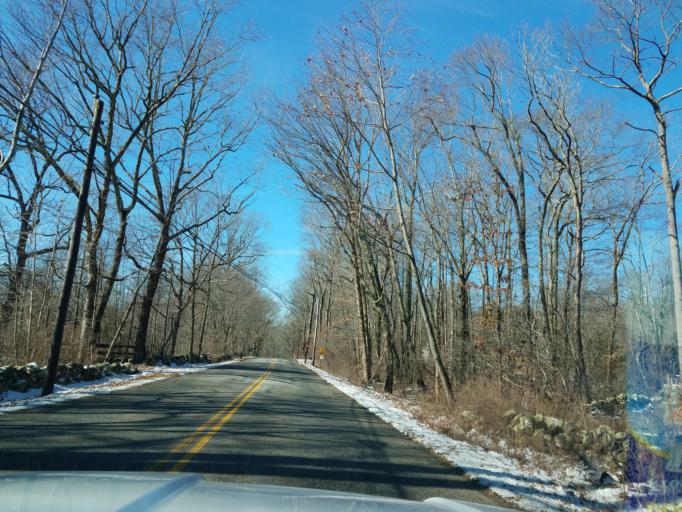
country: US
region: Connecticut
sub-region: New London County
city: Old Mystic
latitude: 41.4562
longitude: -71.9294
